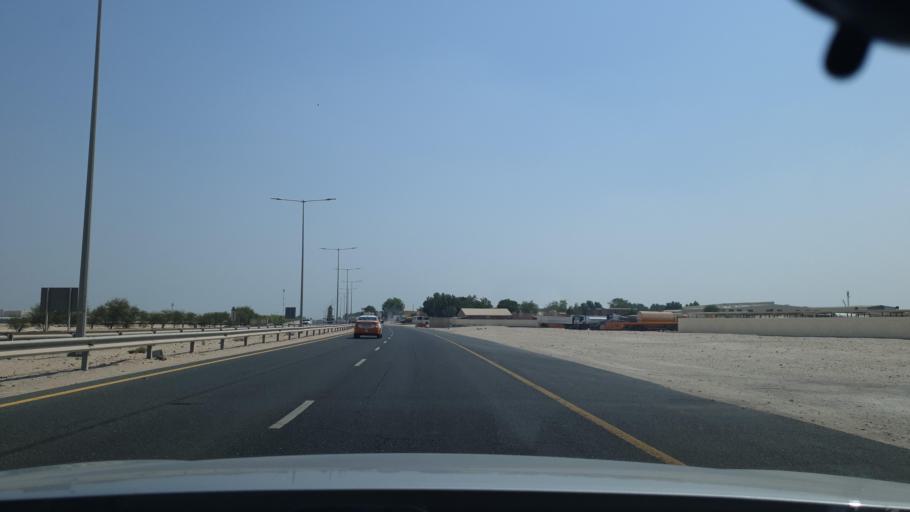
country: QA
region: Al Khawr
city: Al Khawr
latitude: 25.7203
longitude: 51.5005
